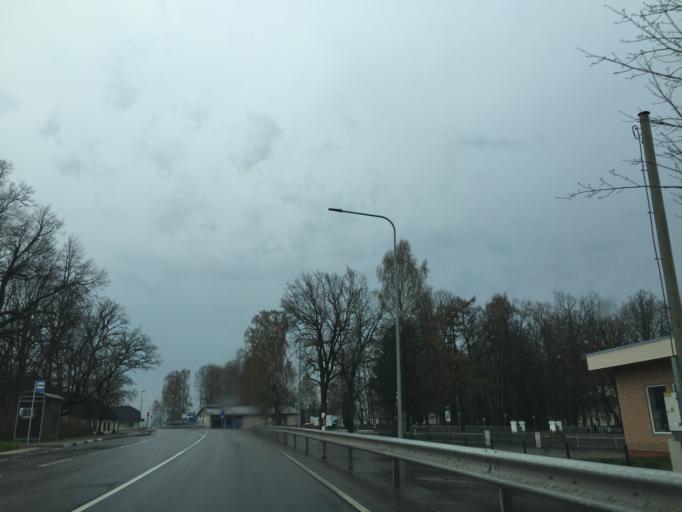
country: EE
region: Tartu
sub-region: UElenurme vald
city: Ulenurme
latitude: 58.2344
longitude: 26.6938
